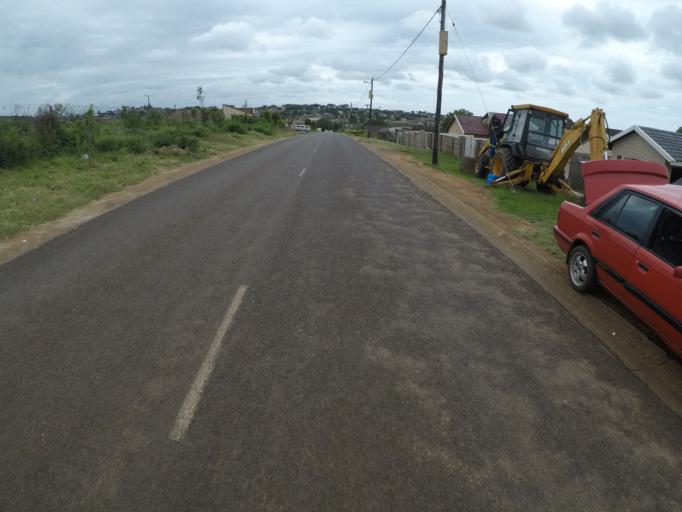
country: ZA
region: KwaZulu-Natal
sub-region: uThungulu District Municipality
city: Empangeni
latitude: -28.7788
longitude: 31.8529
